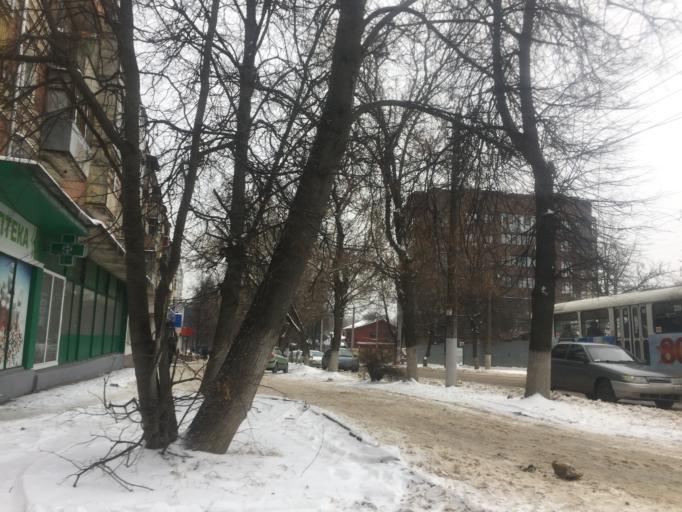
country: RU
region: Tula
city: Tula
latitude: 54.1699
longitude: 37.5999
